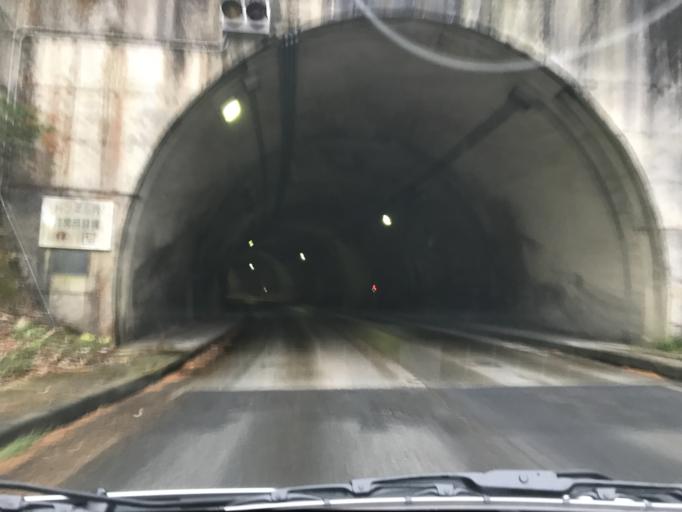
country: JP
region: Iwate
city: Tono
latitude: 39.1755
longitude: 141.3691
